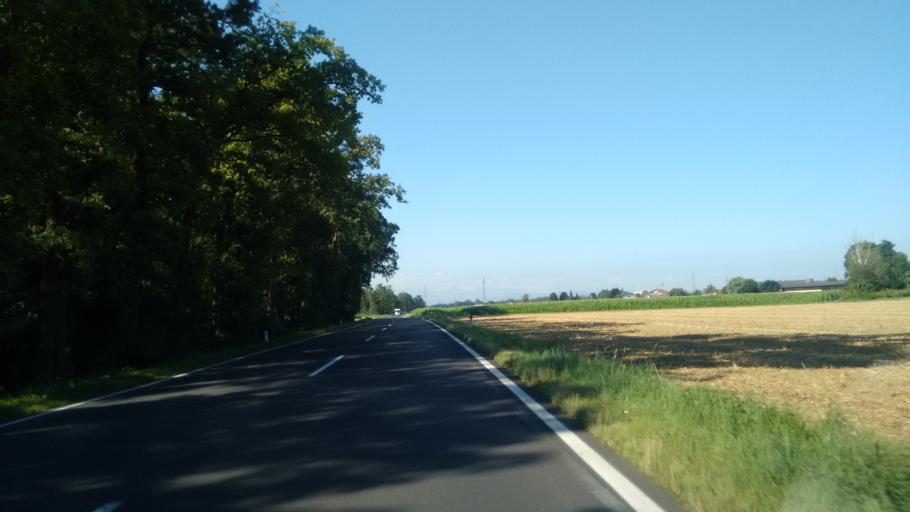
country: AT
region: Upper Austria
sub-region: Wels-Land
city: Gunskirchen
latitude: 48.1142
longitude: 13.9335
